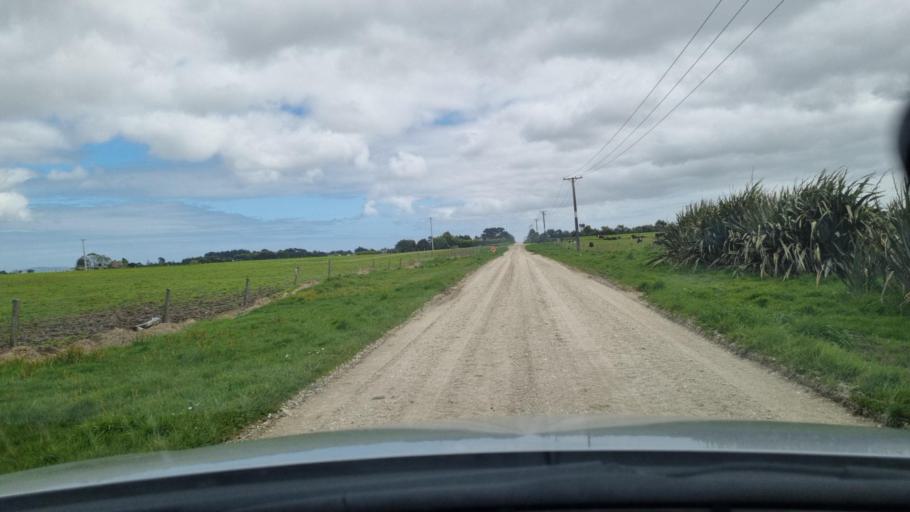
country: NZ
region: Southland
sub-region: Invercargill City
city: Invercargill
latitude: -46.4433
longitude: 168.4168
